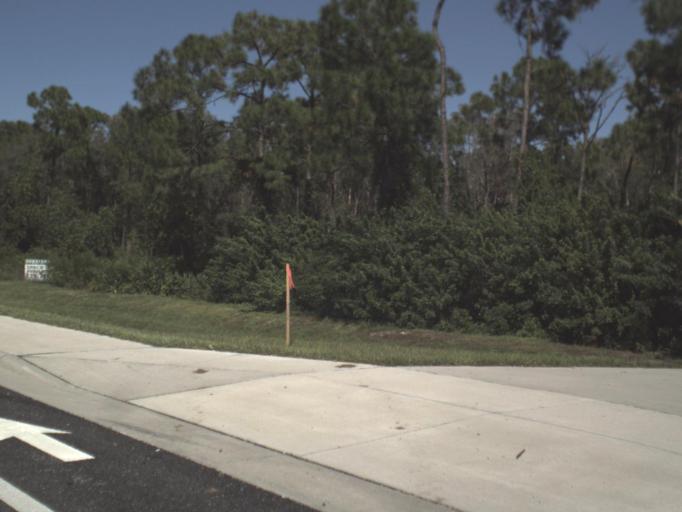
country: US
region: Florida
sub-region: Lee County
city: Estero
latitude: 26.4436
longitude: -81.8116
